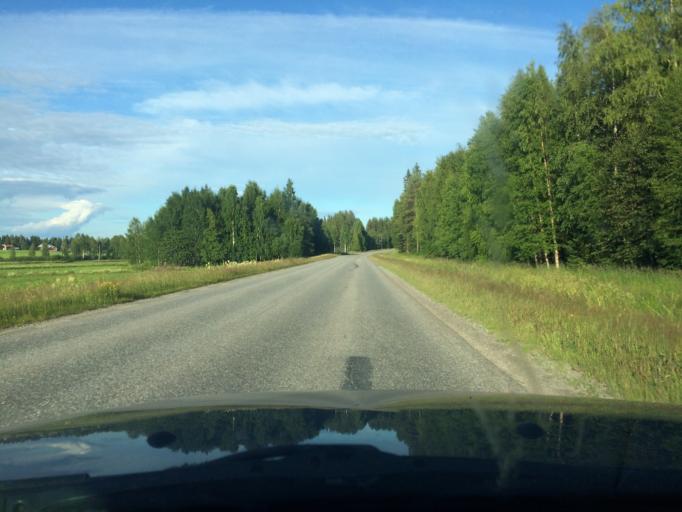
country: SE
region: Norrbotten
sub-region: Pitea Kommun
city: Roknas
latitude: 65.3193
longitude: 21.2730
